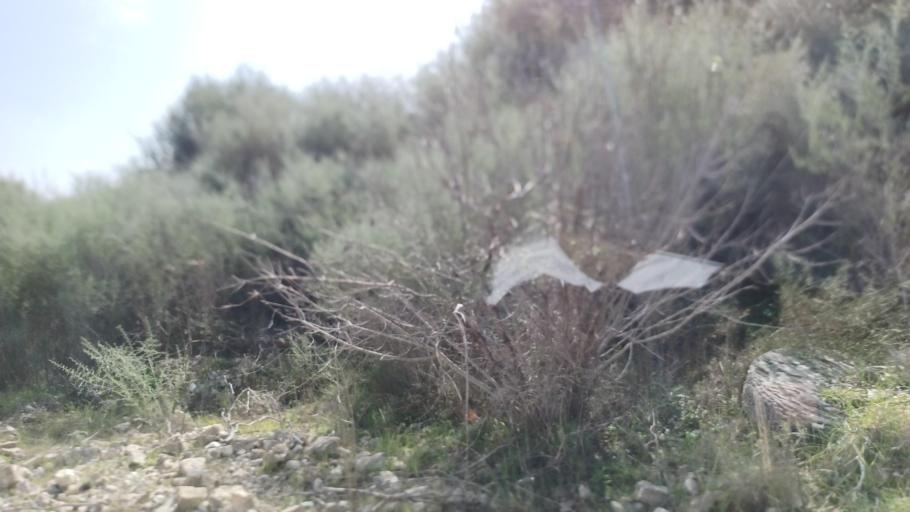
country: CY
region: Limassol
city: Pachna
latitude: 34.8047
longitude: 32.6891
